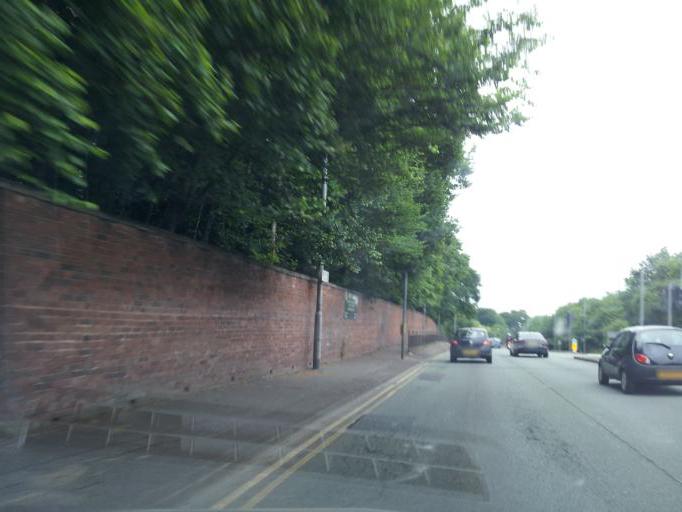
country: GB
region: England
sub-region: Manchester
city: Crumpsall
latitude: 53.5329
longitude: -2.2449
